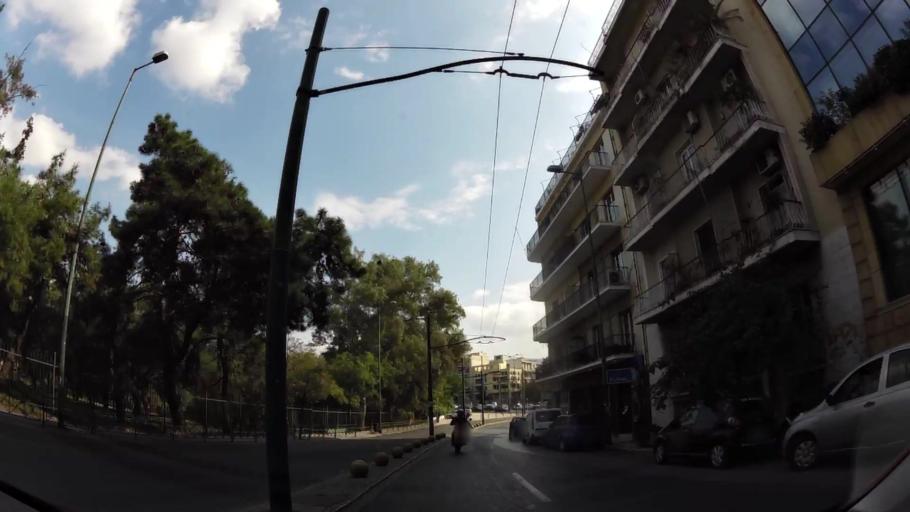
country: GR
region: Attica
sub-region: Nomarchia Athinas
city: Dhafni
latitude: 37.9679
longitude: 23.7326
